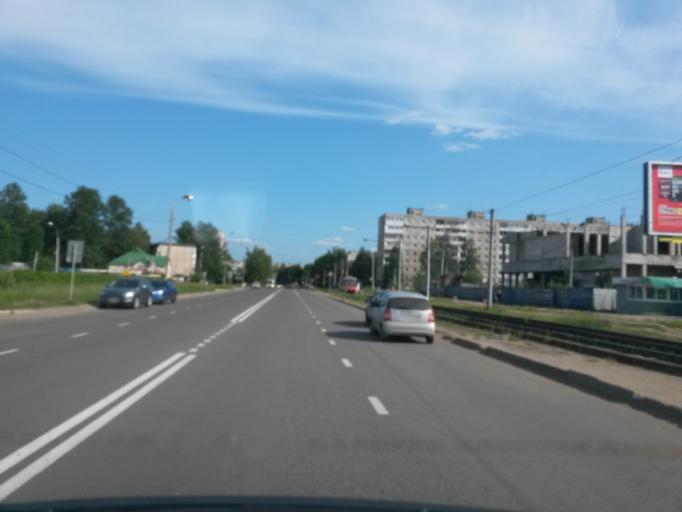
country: RU
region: Jaroslavl
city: Yaroslavl
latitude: 57.6854
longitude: 39.7673
